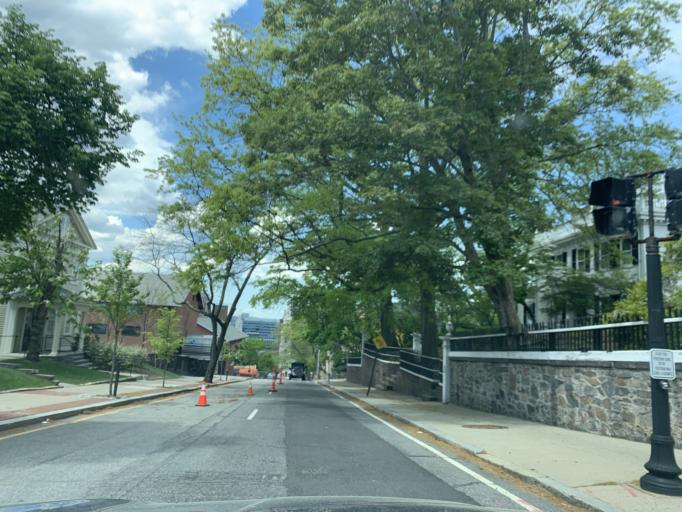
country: US
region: Rhode Island
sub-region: Providence County
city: Providence
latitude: 41.8277
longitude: -71.4048
